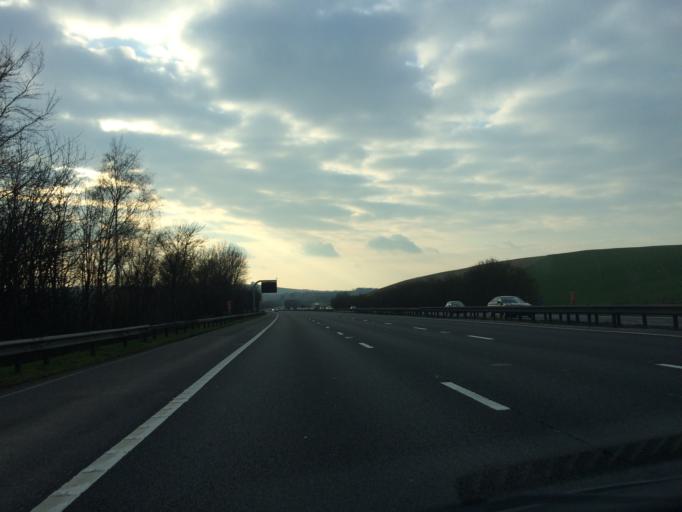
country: GB
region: England
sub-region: Wiltshire
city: Aldbourne
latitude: 51.5139
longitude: -1.6346
